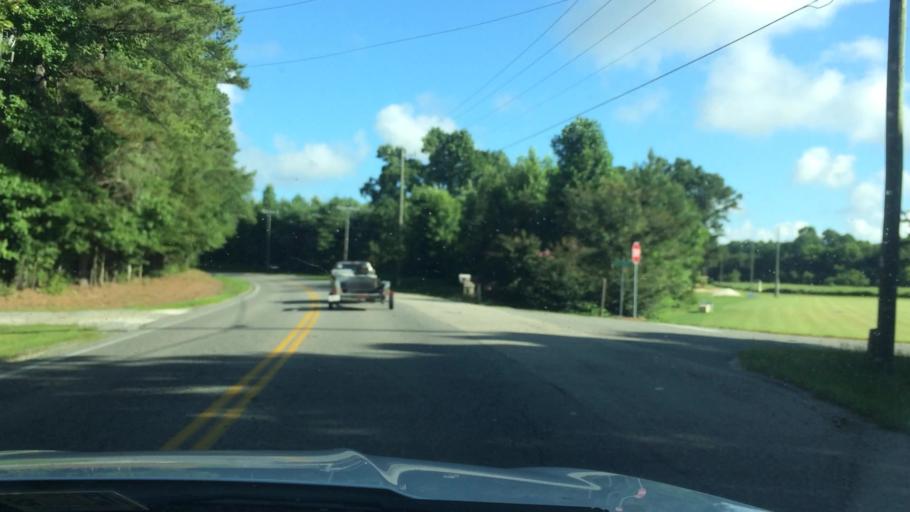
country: US
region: Virginia
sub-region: Middlesex County
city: Deltaville
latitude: 37.5348
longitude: -76.4224
